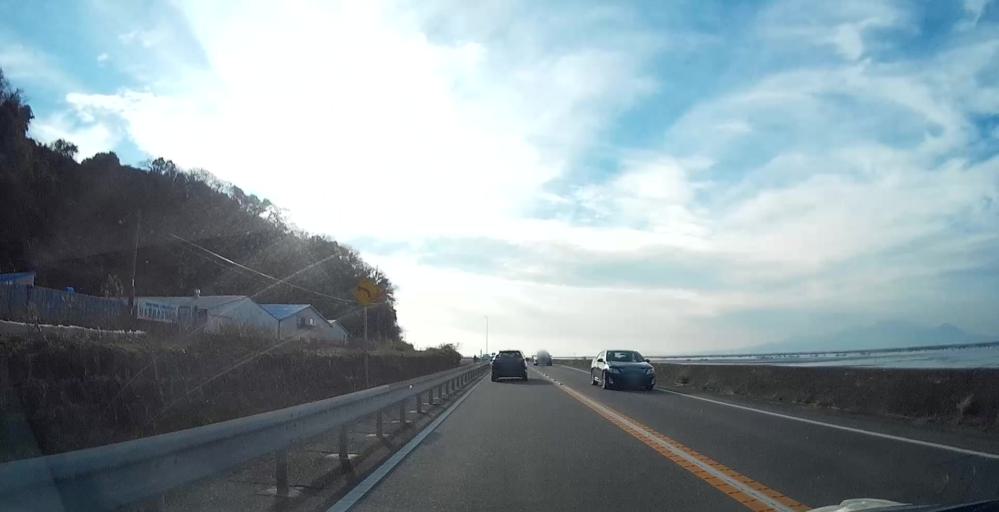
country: JP
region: Kumamoto
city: Uto
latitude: 32.6995
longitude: 130.5686
